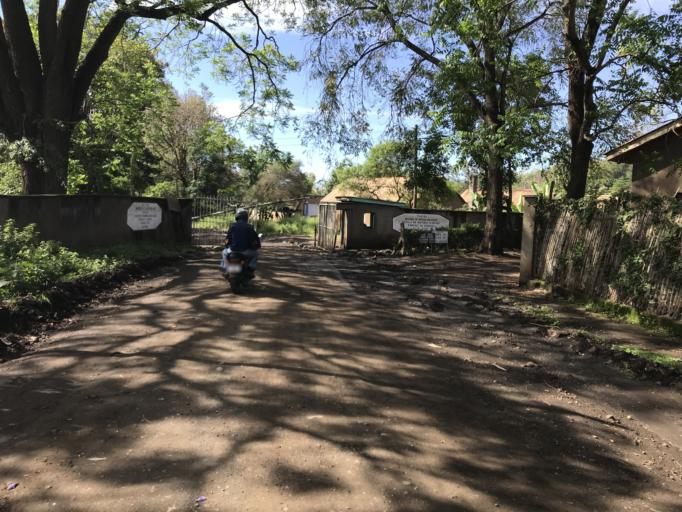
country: TZ
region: Arusha
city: Nkoaranga
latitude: -3.3829
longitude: 36.7954
